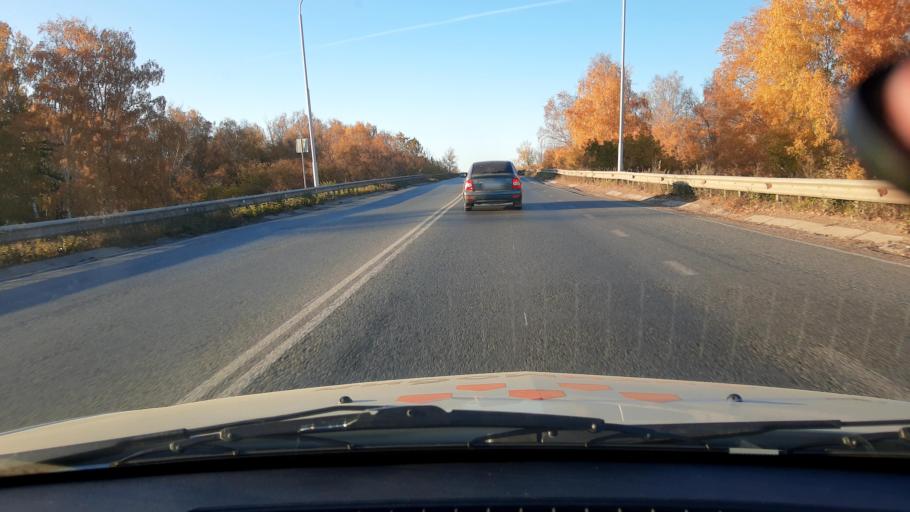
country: RU
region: Bashkortostan
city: Iglino
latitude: 54.7730
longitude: 56.2575
